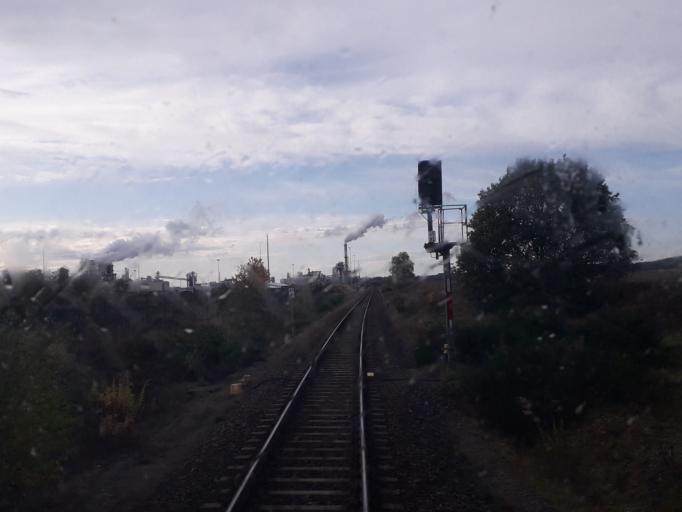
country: DE
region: Brandenburg
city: Heiligengrabe
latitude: 53.1513
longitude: 12.3919
